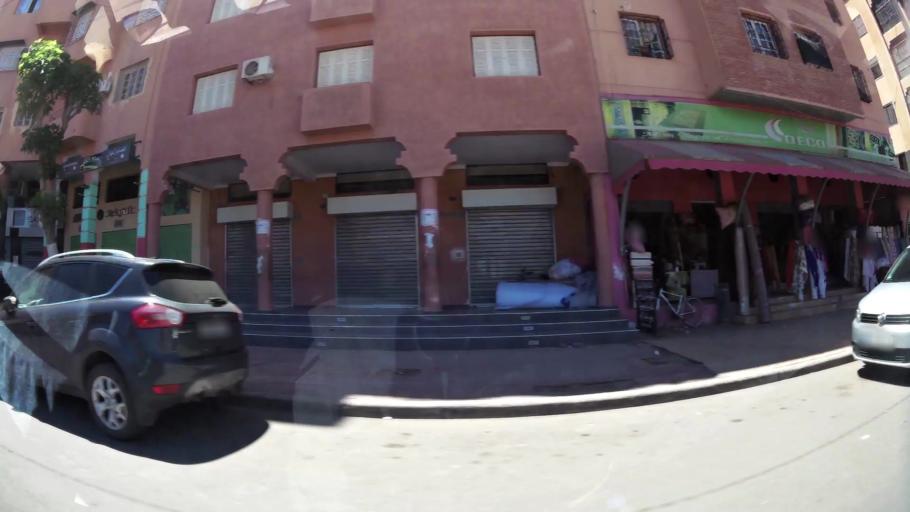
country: MA
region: Marrakech-Tensift-Al Haouz
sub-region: Marrakech
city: Marrakesh
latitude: 31.6331
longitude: -8.0549
